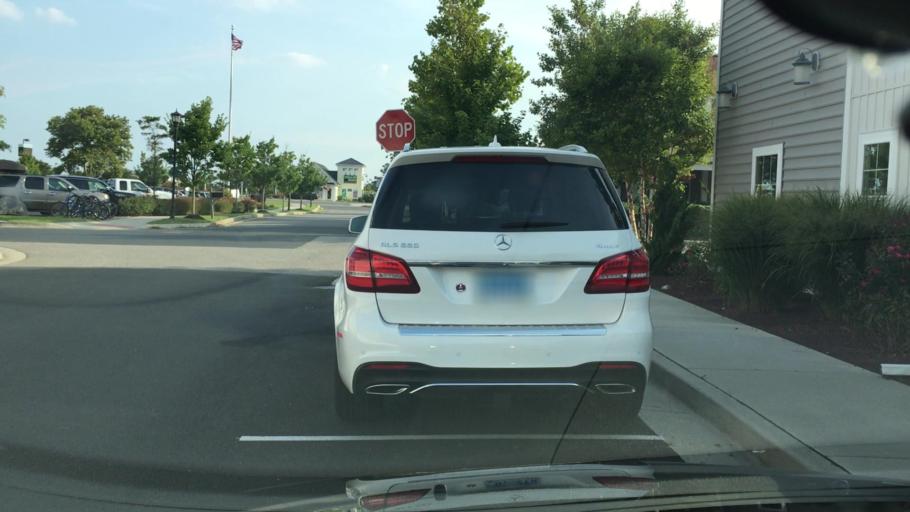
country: US
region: Maryland
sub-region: Worcester County
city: West Ocean City
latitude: 38.3367
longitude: -75.1032
